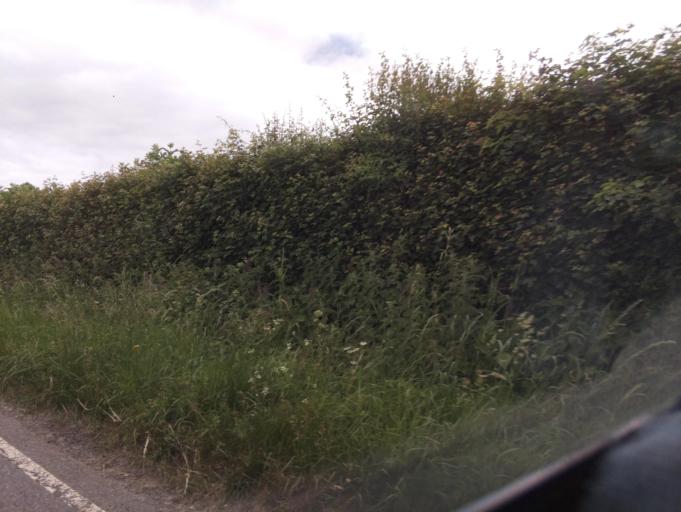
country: GB
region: England
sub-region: Dorset
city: Sherborne
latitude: 50.9673
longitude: -2.5141
